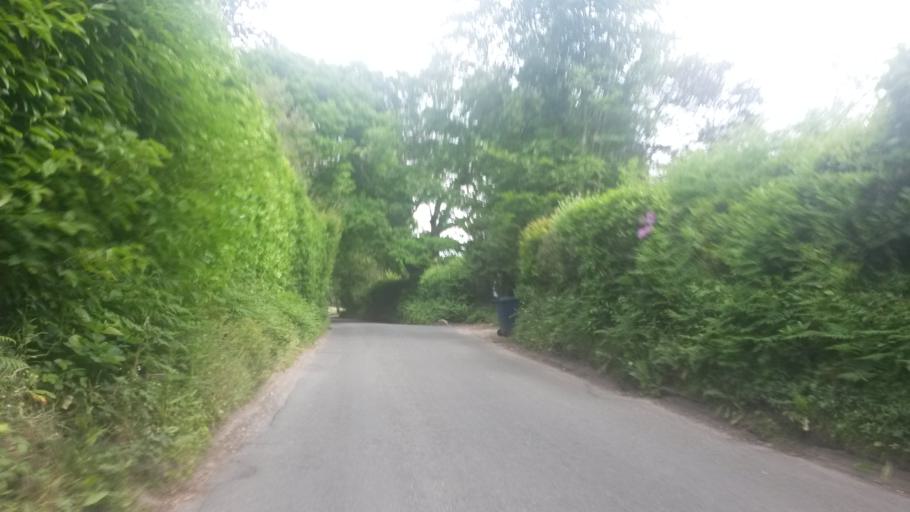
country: GB
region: England
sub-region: Surrey
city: Haslemere
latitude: 51.0815
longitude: -0.7084
